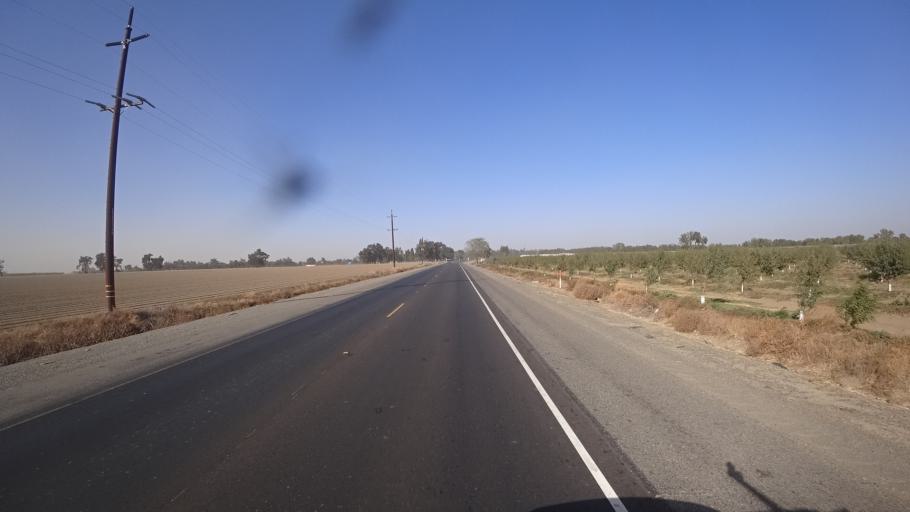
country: US
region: California
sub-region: Yolo County
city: Woodland
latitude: 38.7863
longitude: -121.7284
